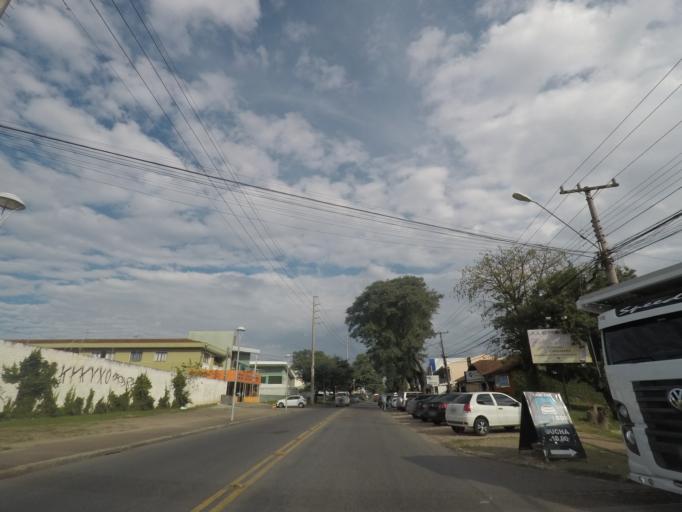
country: BR
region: Parana
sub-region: Sao Jose Dos Pinhais
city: Sao Jose dos Pinhais
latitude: -25.5395
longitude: -49.2946
